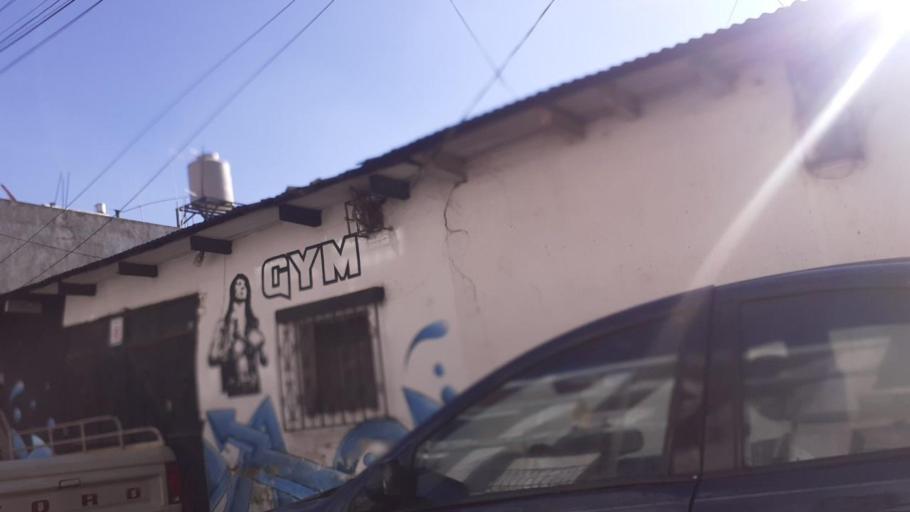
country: GT
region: Quetzaltenango
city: Ostuncalco
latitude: 14.8662
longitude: -91.6208
